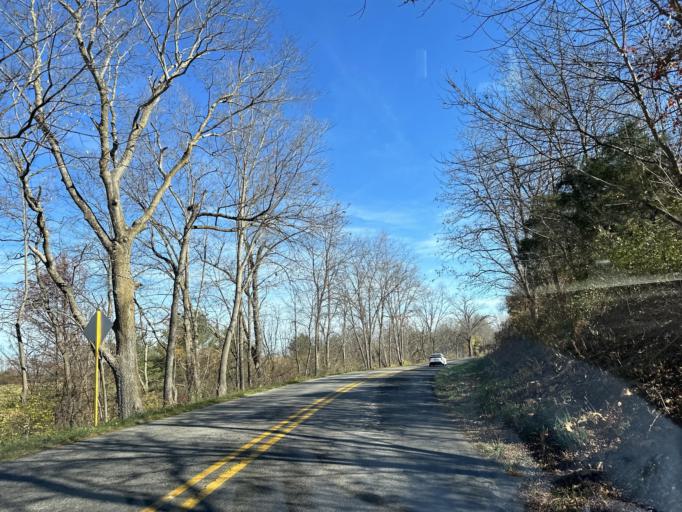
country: US
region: Virginia
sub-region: Augusta County
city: Fishersville
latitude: 38.1131
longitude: -78.9603
